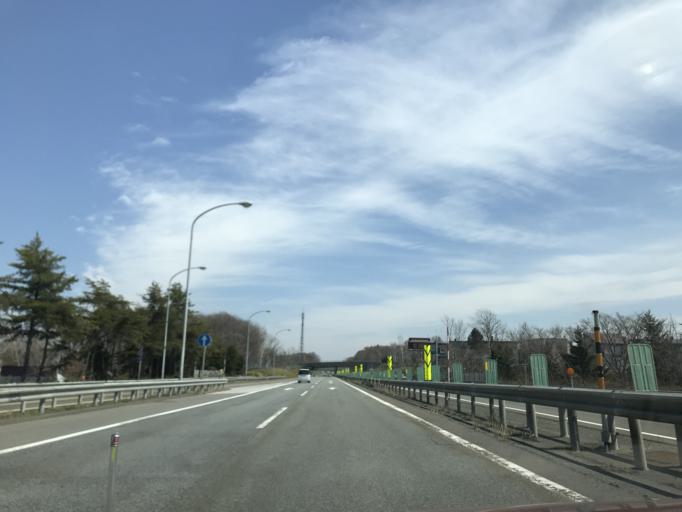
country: JP
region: Hokkaido
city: Iwamizawa
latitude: 43.1758
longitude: 141.7685
